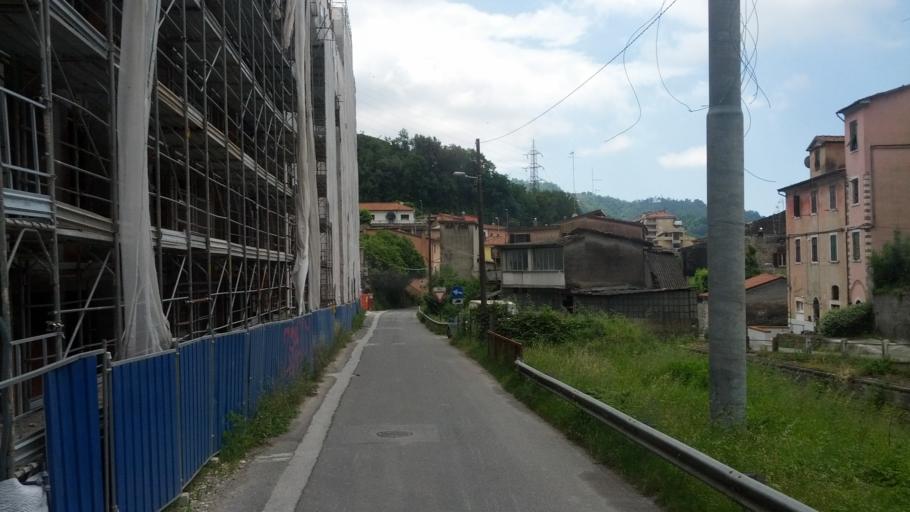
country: IT
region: Tuscany
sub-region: Provincia di Massa-Carrara
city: Carrara
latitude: 44.0836
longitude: 10.1033
